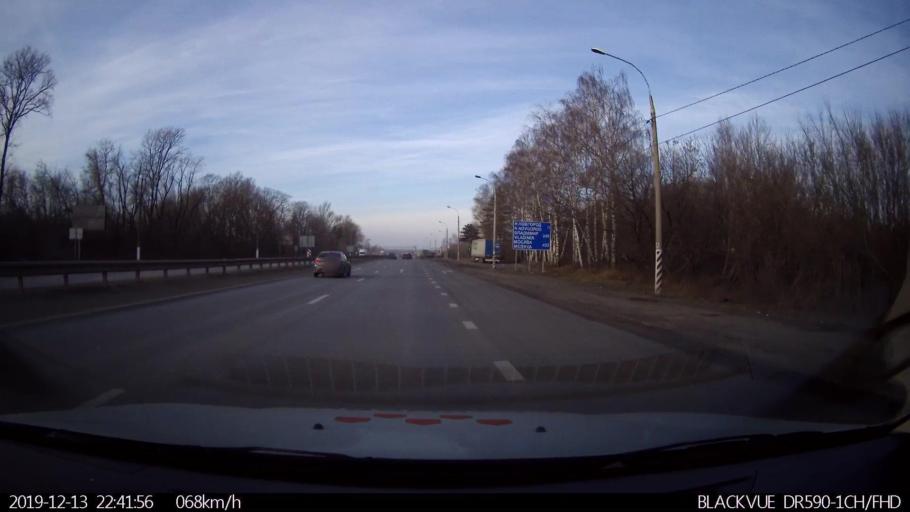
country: RU
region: Nizjnij Novgorod
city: Kstovo
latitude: 56.1861
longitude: 44.1418
